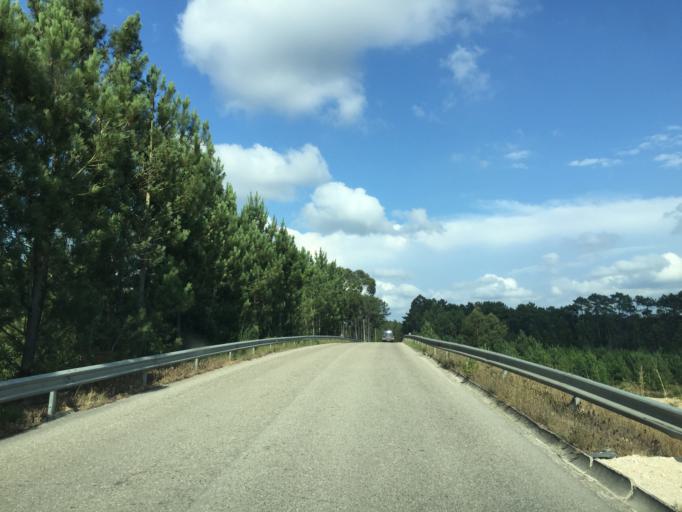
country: PT
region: Leiria
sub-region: Leiria
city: Monte Redondo
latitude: 39.9458
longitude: -8.8035
